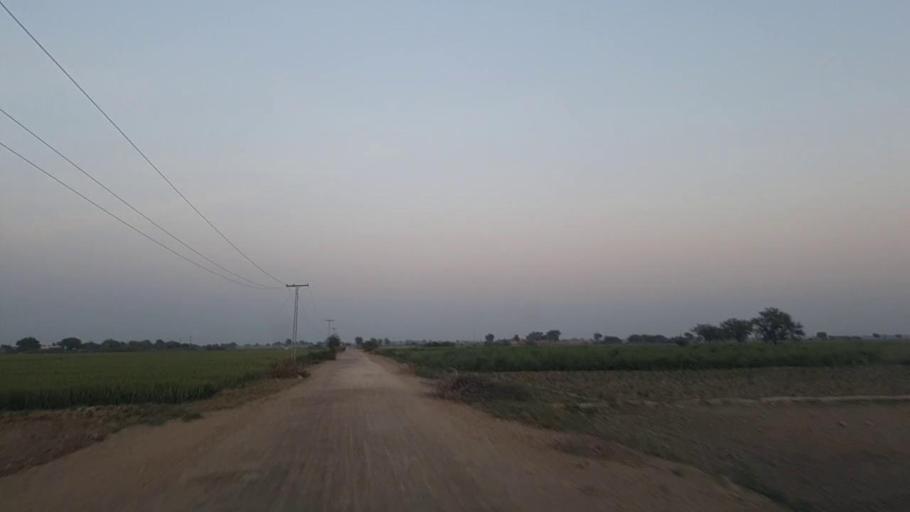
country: PK
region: Sindh
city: Naukot
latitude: 24.9966
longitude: 69.4263
